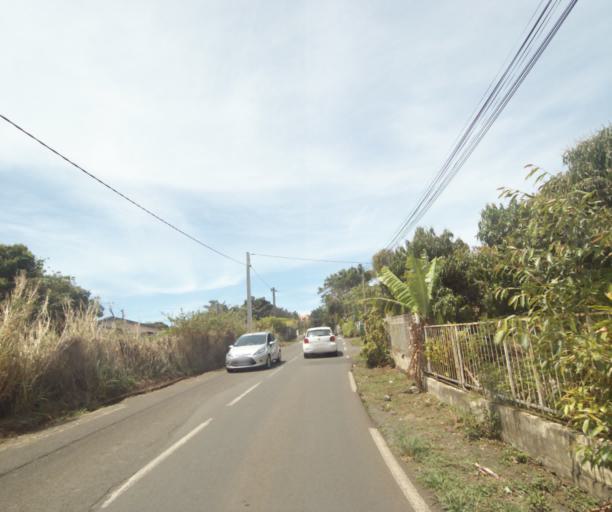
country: RE
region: Reunion
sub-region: Reunion
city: Saint-Paul
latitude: -21.0474
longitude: 55.2787
